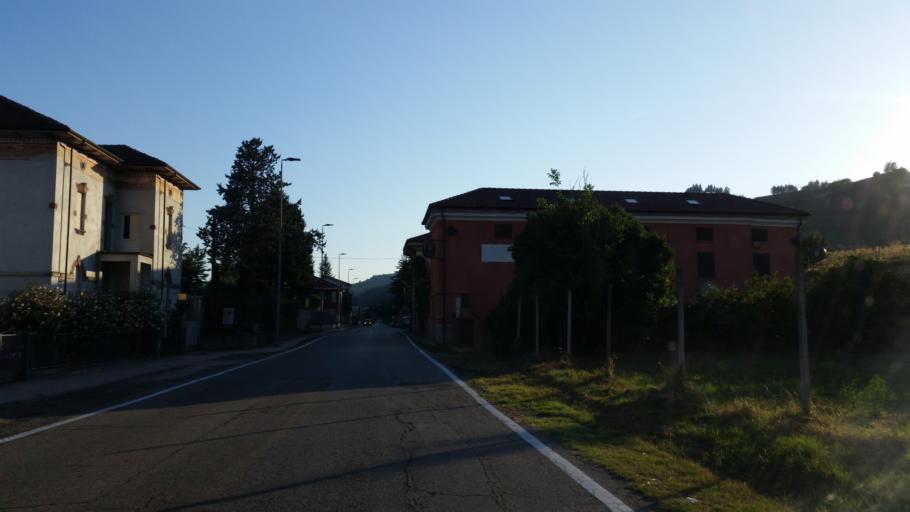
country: IT
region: Piedmont
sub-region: Provincia di Cuneo
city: Santo Stefano Belbo
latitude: 44.7160
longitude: 8.2390
